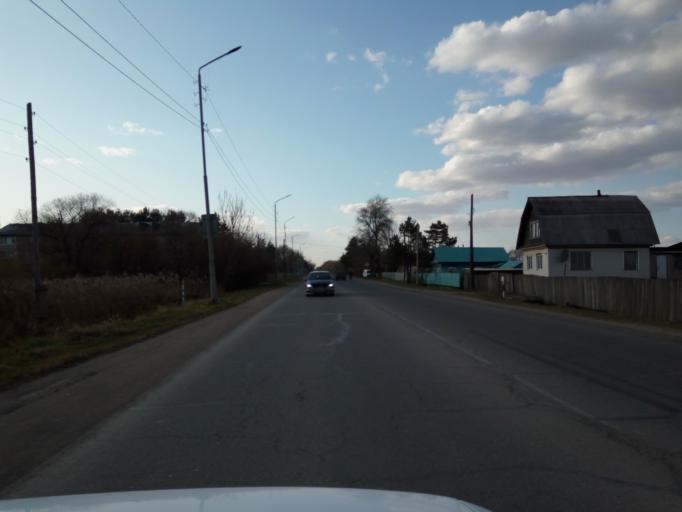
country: RU
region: Primorskiy
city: Dal'nerechensk
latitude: 45.9188
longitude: 133.7593
